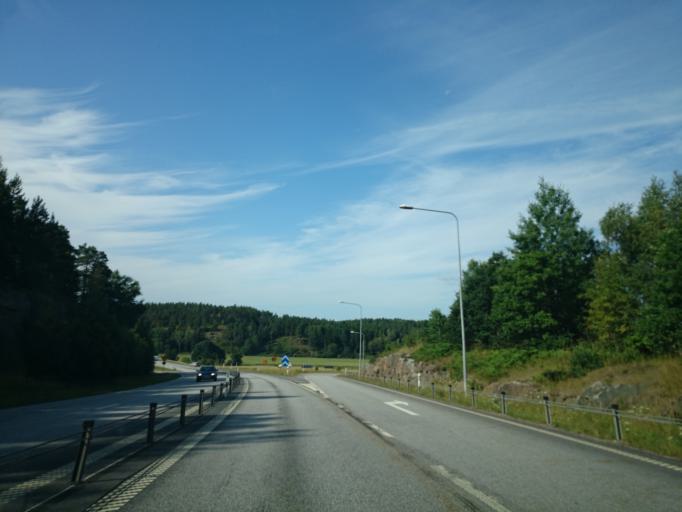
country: SE
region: Kalmar
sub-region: Vasterviks Kommun
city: Gamleby
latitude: 57.9106
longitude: 16.3880
